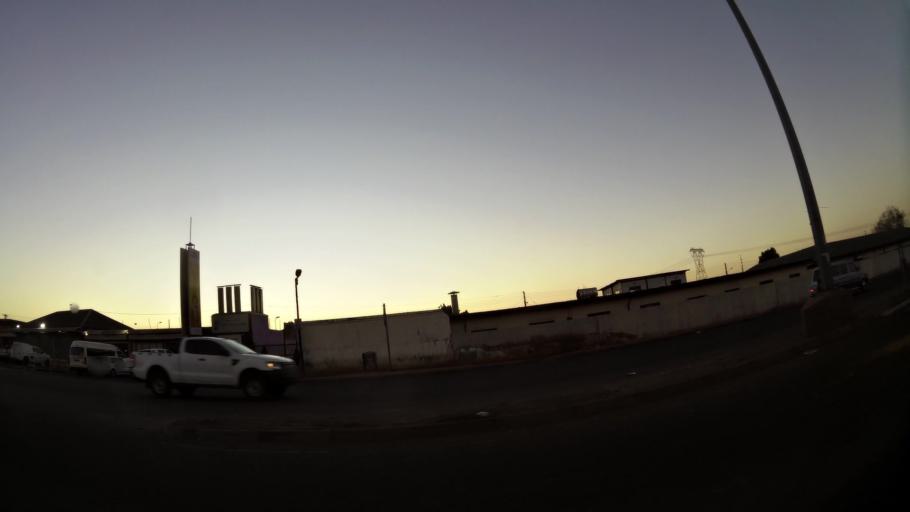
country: ZA
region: North-West
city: Ga-Rankuwa
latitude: -25.5879
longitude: 27.9864
